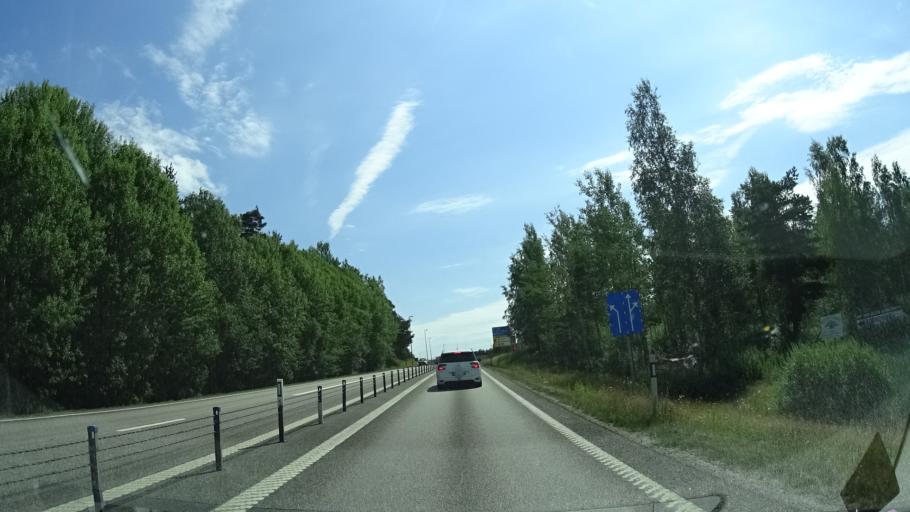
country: SE
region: Vaermland
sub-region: Kristinehamns Kommun
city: Kristinehamn
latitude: 59.3714
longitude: 14.0080
